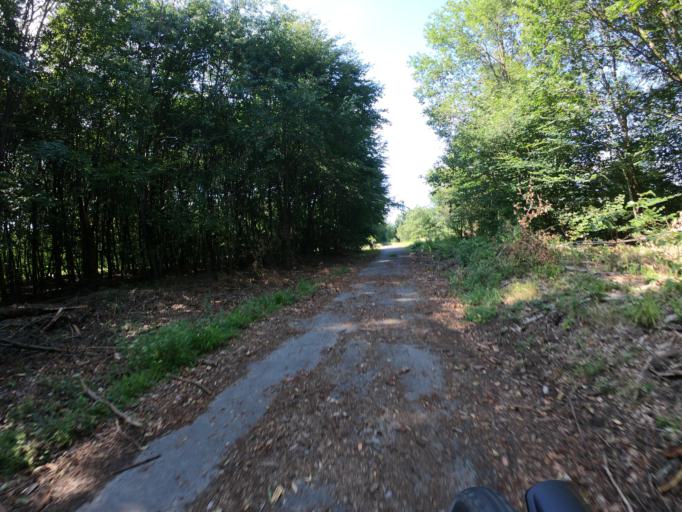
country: DE
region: Hesse
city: Morfelden-Walldorf
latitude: 49.9936
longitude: 8.6141
